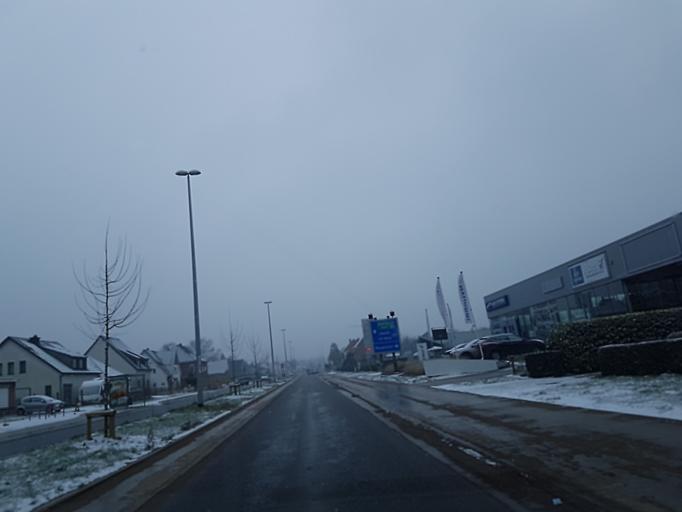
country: BE
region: Flanders
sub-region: Provincie Oost-Vlaanderen
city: Sint-Niklaas
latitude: 51.1813
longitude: 4.1959
